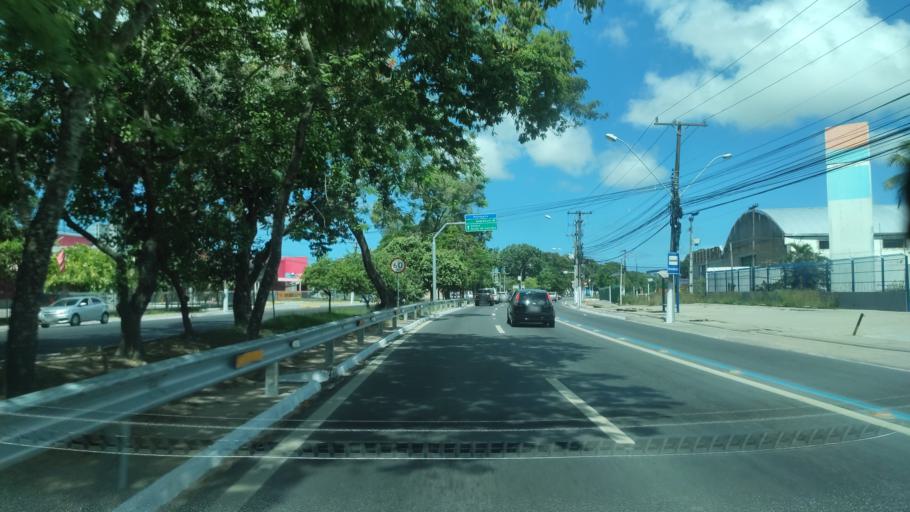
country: BR
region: Alagoas
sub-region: Maceio
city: Maceio
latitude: -9.5945
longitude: -35.7528
